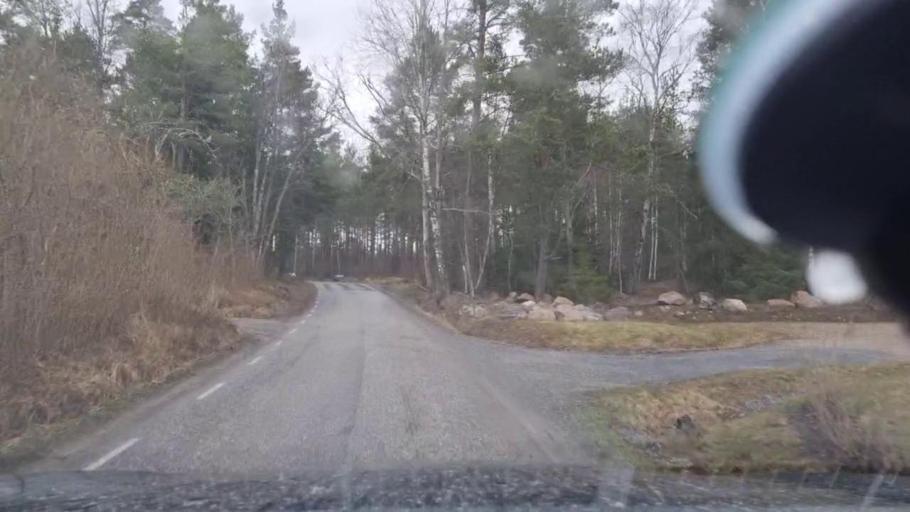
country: SE
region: Stockholm
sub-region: Vallentuna Kommun
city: Vallentuna
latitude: 59.5087
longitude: 18.0098
